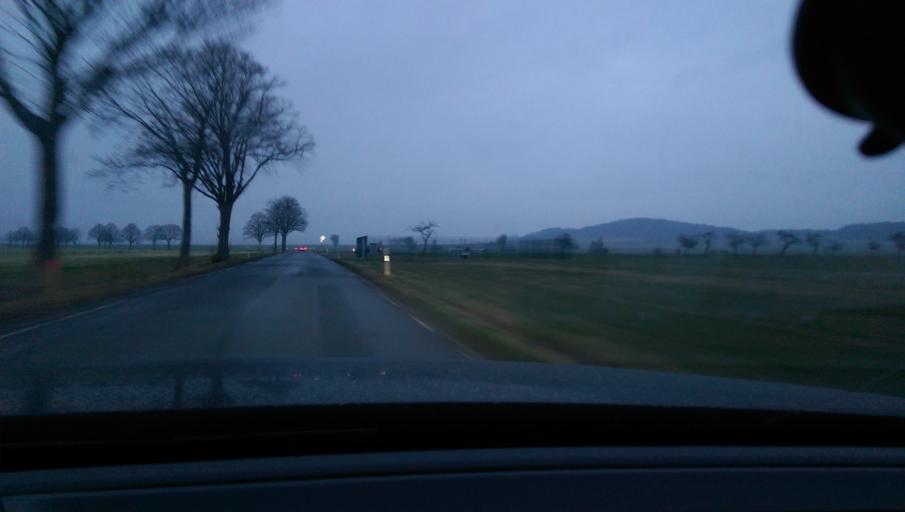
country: DE
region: Lower Saxony
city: Wennigsen
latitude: 52.3019
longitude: 9.5680
